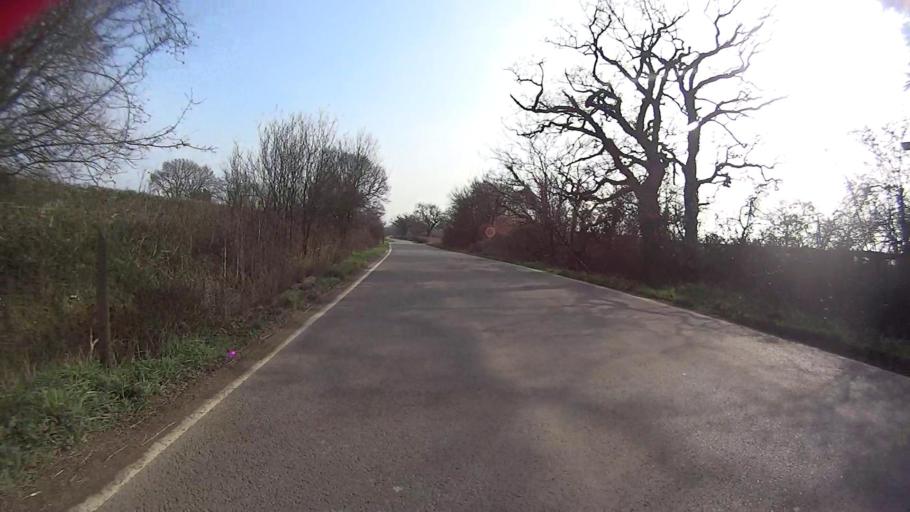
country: GB
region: England
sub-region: Surrey
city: Felbridge
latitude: 51.1842
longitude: -0.0691
